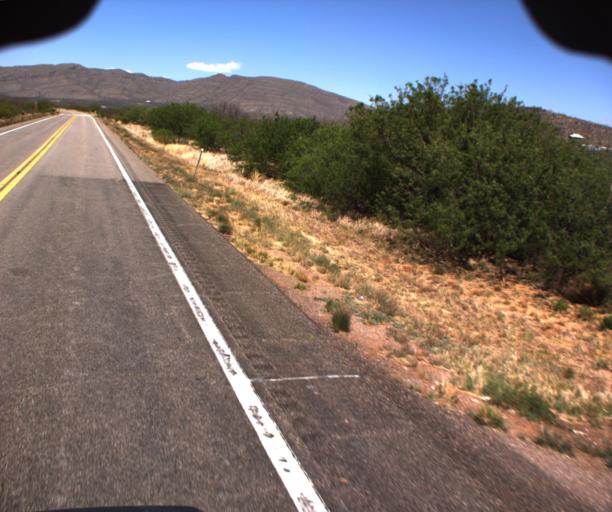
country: US
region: Arizona
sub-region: Cochise County
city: Bisbee
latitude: 31.5467
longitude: -110.0109
